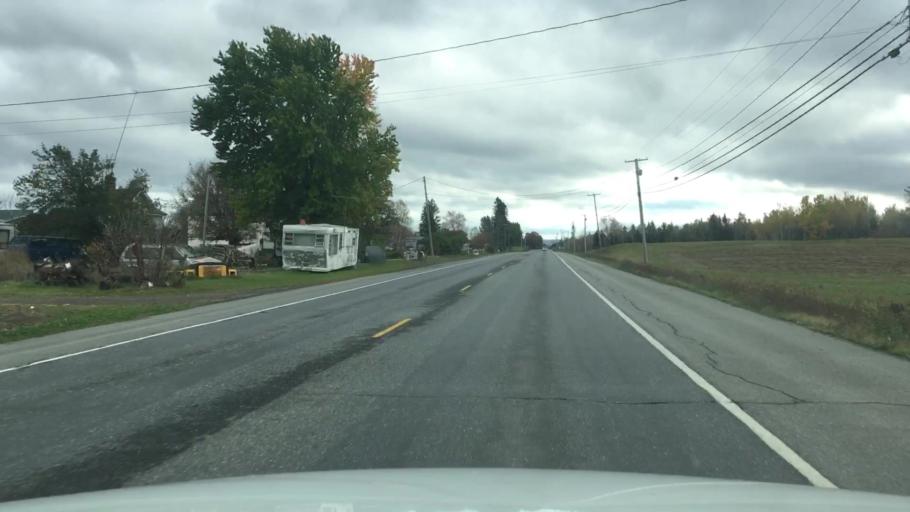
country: US
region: Maine
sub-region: Aroostook County
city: Houlton
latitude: 46.1881
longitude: -67.8413
